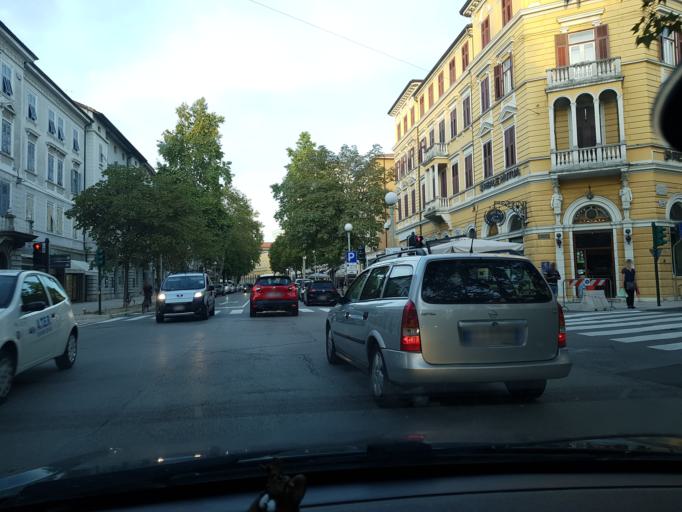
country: IT
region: Friuli Venezia Giulia
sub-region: Provincia di Gorizia
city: Gorizia
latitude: 45.9413
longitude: 13.6178
